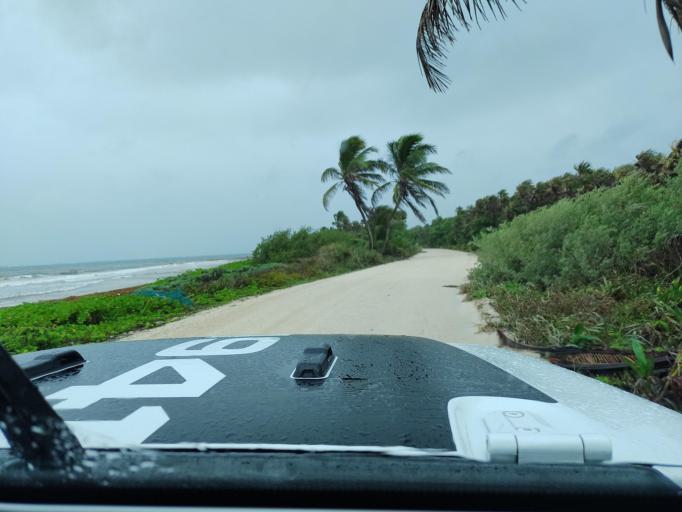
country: MX
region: Quintana Roo
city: Tulum
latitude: 19.9791
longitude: -87.4683
